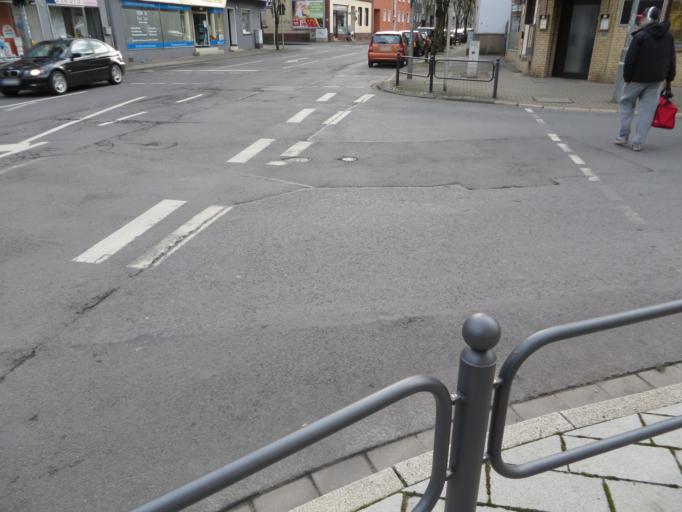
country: DE
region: North Rhine-Westphalia
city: Witten
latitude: 51.4447
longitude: 7.3673
